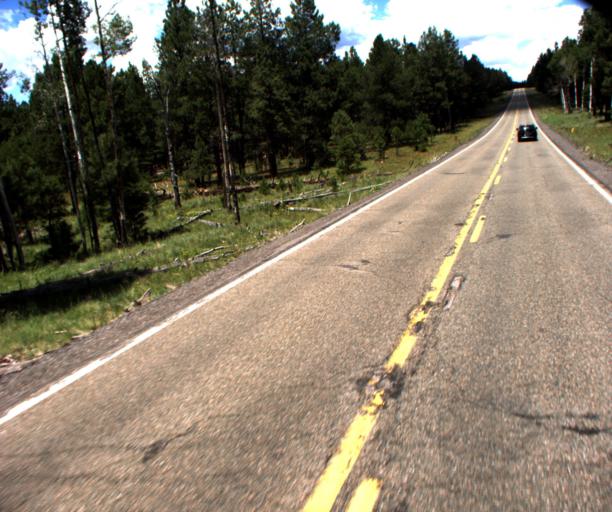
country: US
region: Arizona
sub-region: Coconino County
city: Parks
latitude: 35.3411
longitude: -111.7875
